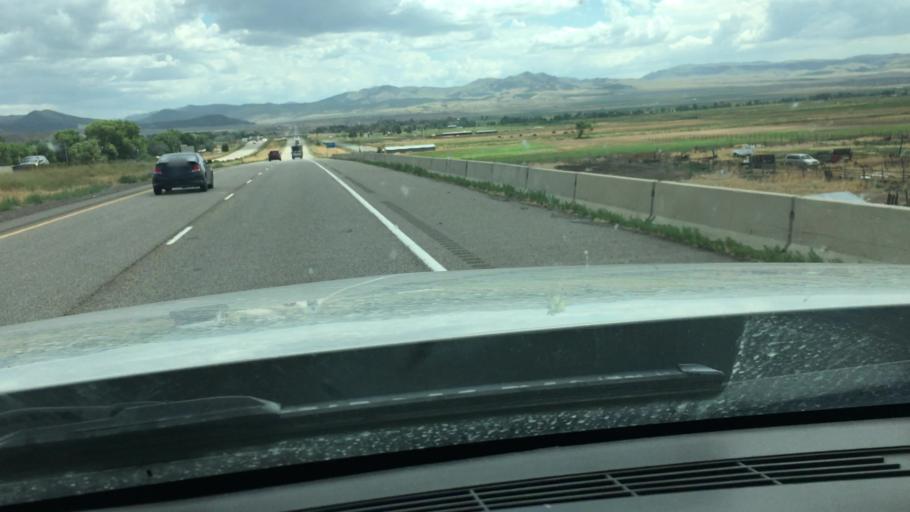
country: US
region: Utah
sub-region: Beaver County
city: Beaver
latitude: 38.2813
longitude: -112.6507
